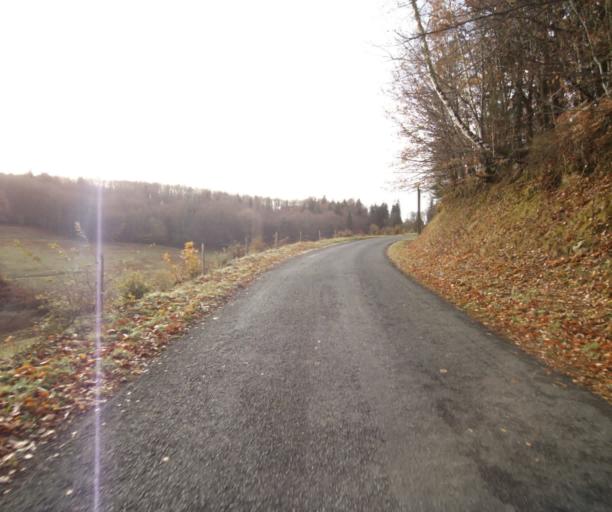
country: FR
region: Limousin
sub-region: Departement de la Correze
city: Cornil
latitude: 45.2169
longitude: 1.7157
